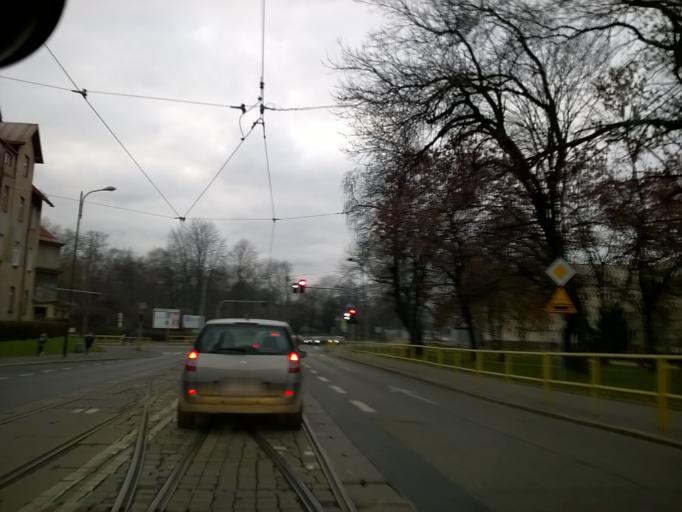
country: PL
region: Silesian Voivodeship
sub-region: Swietochlowice
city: Swietochlowice
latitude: 50.2863
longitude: 18.9276
